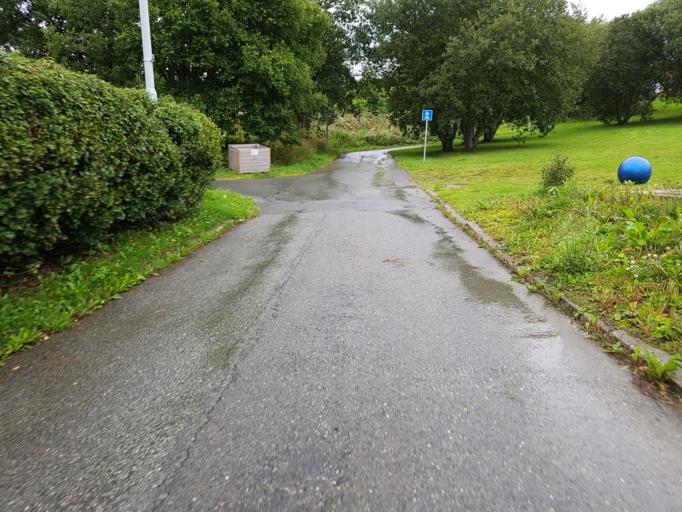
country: NO
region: Sor-Trondelag
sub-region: Trondheim
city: Trondheim
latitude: 63.3940
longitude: 10.4365
